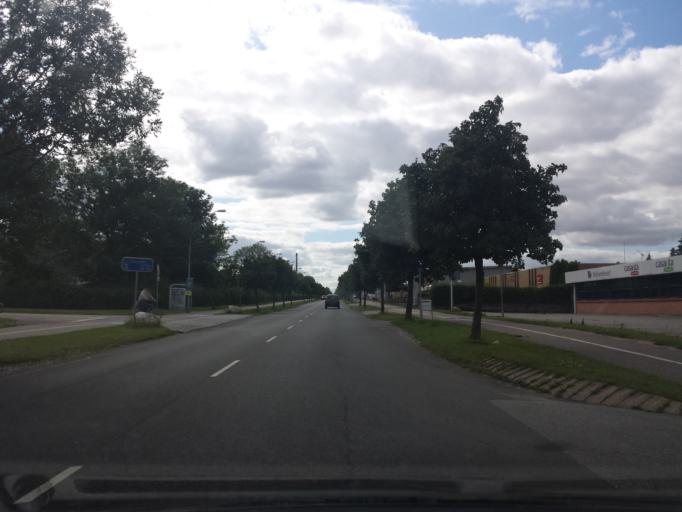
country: DK
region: South Denmark
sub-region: Sonderborg Kommune
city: Sonderborg
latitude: 54.9234
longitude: 9.8010
